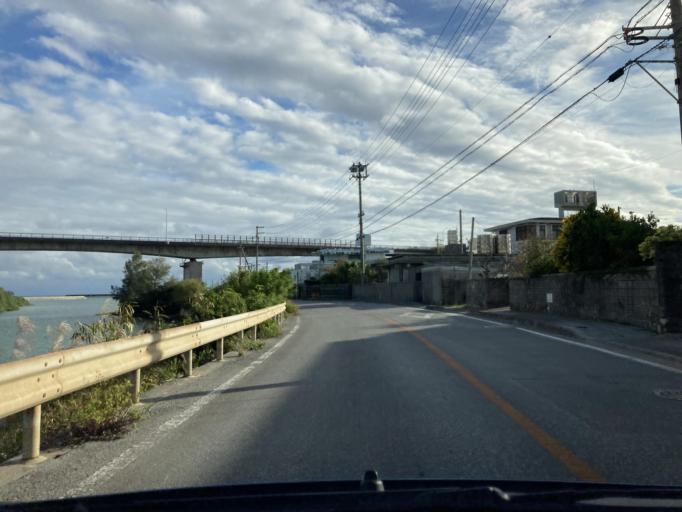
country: JP
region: Okinawa
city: Itoman
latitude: 26.1309
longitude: 127.7596
